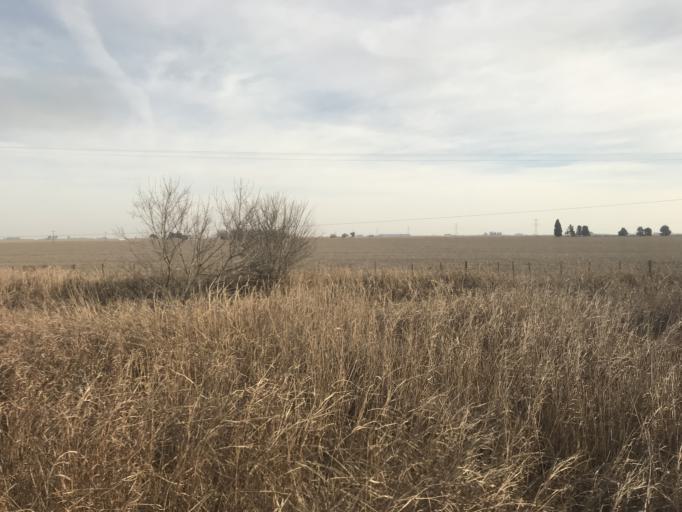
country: AR
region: Cordoba
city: Pilar
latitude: -31.7148
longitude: -63.8573
